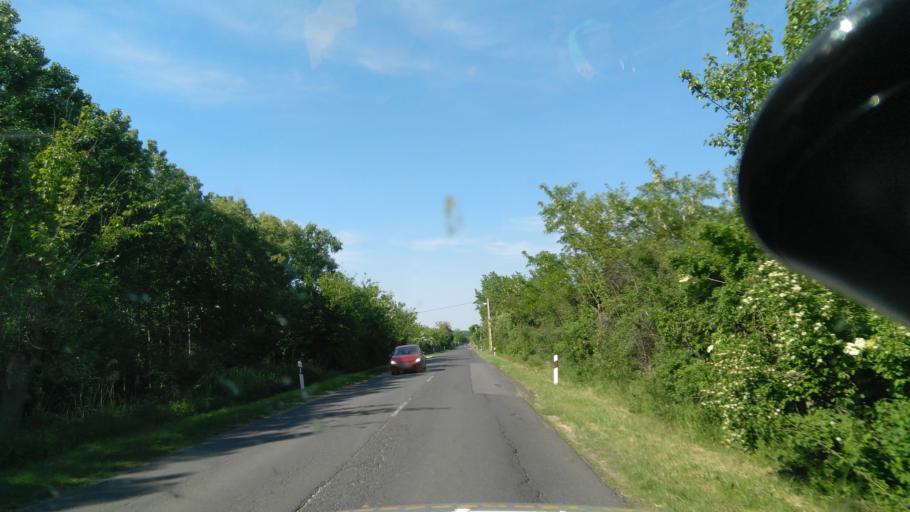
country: HU
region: Bekes
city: Gyula
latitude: 46.6925
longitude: 21.3089
